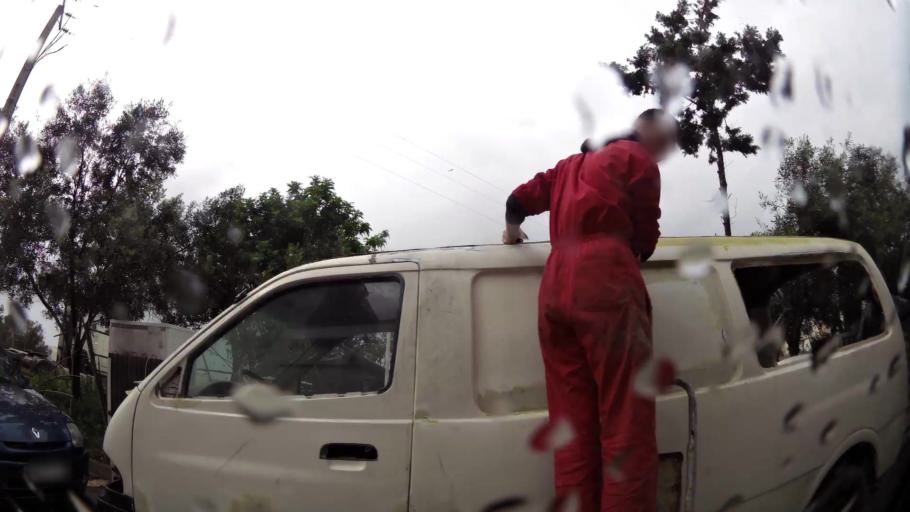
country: MA
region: Grand Casablanca
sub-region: Mediouna
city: Tit Mellil
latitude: 33.6199
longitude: -7.4893
